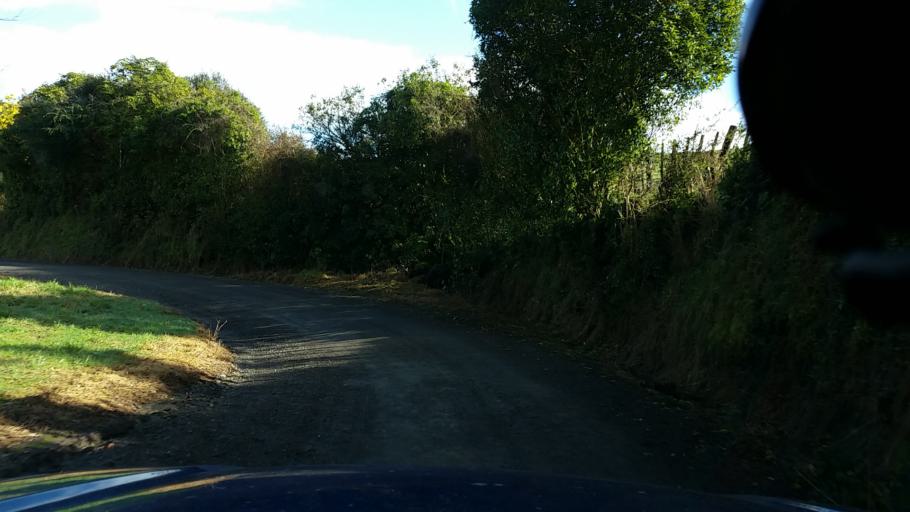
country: NZ
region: Taranaki
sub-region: New Plymouth District
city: Waitara
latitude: -39.0612
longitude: 174.7911
